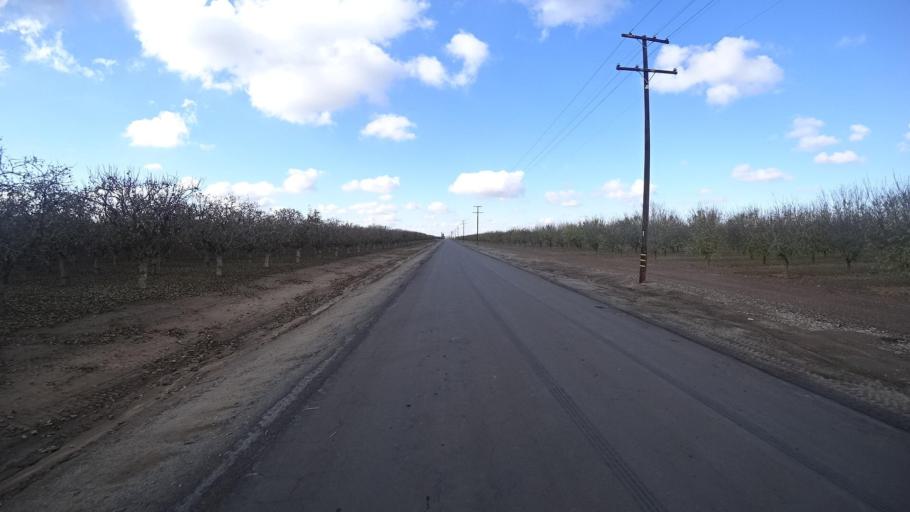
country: US
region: California
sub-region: Kern County
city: McFarland
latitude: 35.6601
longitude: -119.1878
